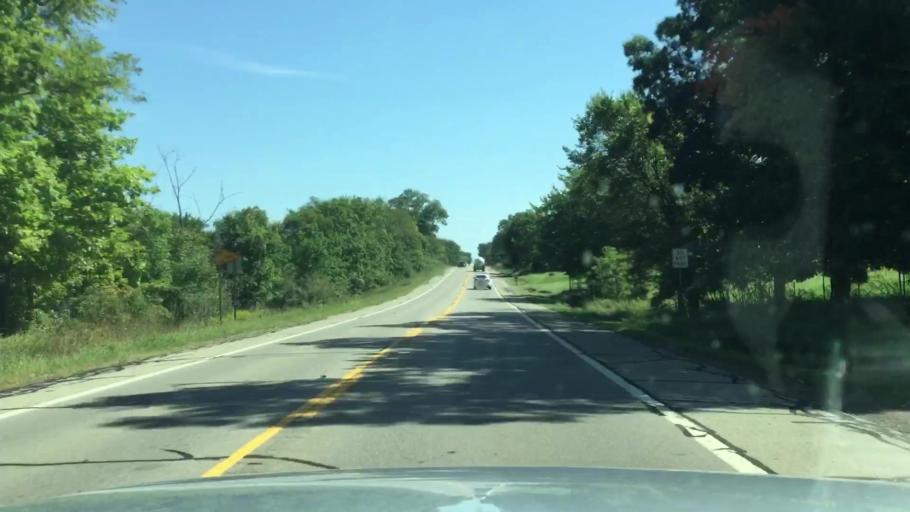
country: US
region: Michigan
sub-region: Washtenaw County
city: Manchester
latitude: 42.0728
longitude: -84.0545
